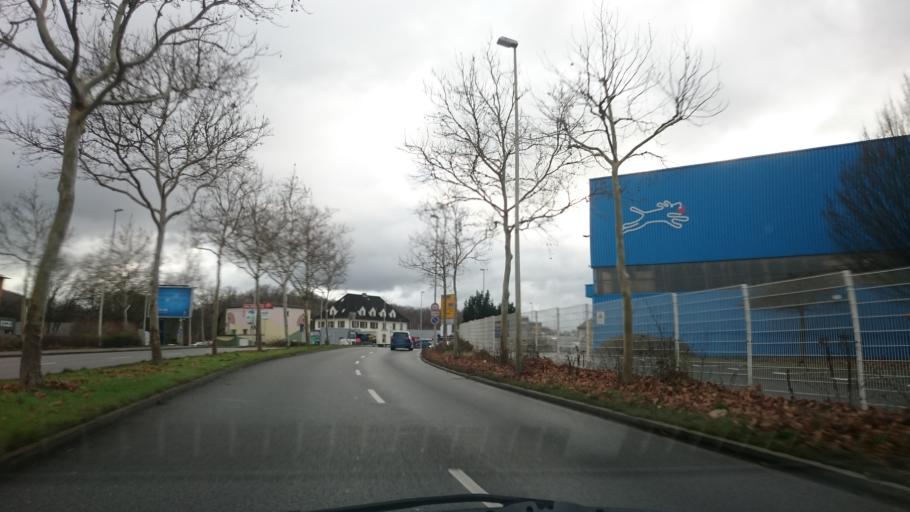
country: DE
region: Saxony
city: Zwickau
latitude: 50.7106
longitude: 12.5022
